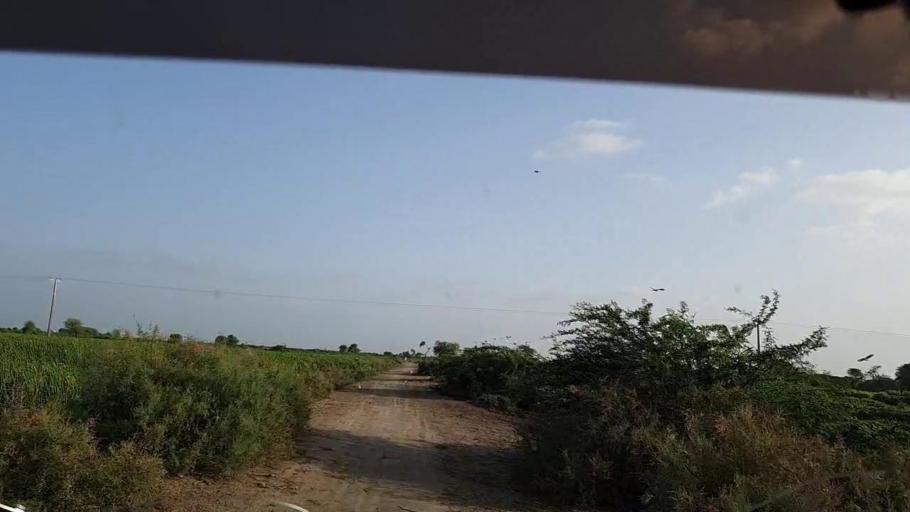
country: PK
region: Sindh
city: Badin
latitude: 24.5534
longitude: 68.8635
